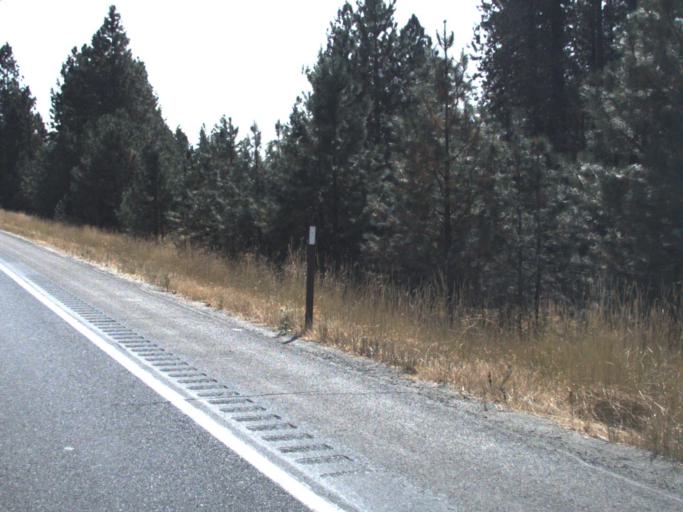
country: US
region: Washington
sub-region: Spokane County
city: Deer Park
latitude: 48.0556
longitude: -117.6172
